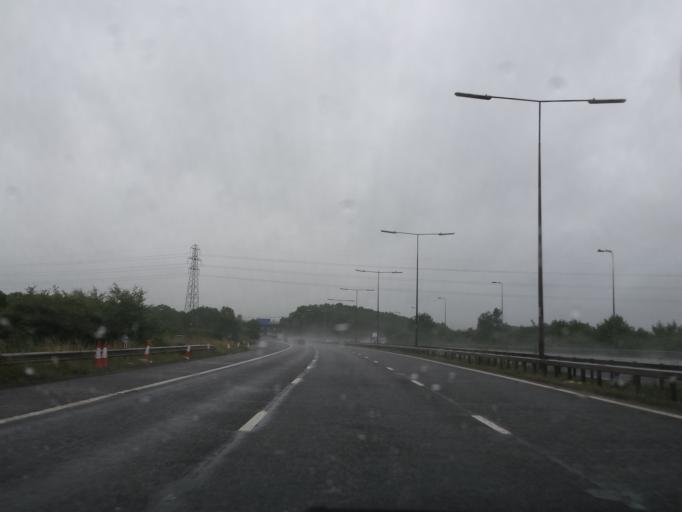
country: GB
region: England
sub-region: Warwickshire
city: Bedworth
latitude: 52.4453
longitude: -1.4253
